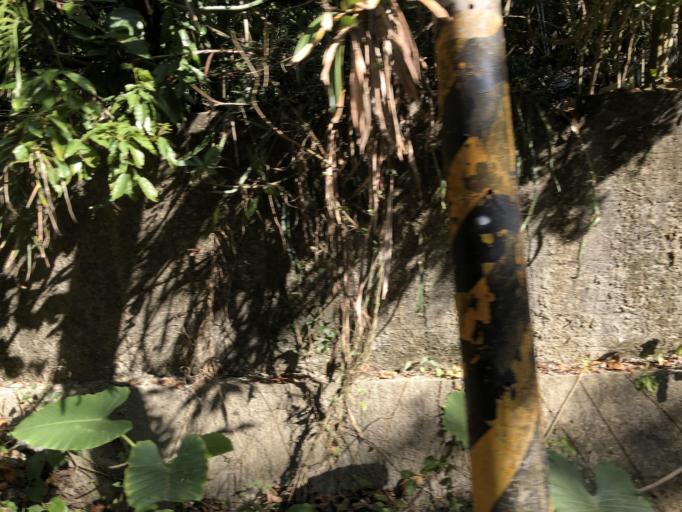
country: TW
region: Taiwan
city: Yujing
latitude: 23.0147
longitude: 120.3983
